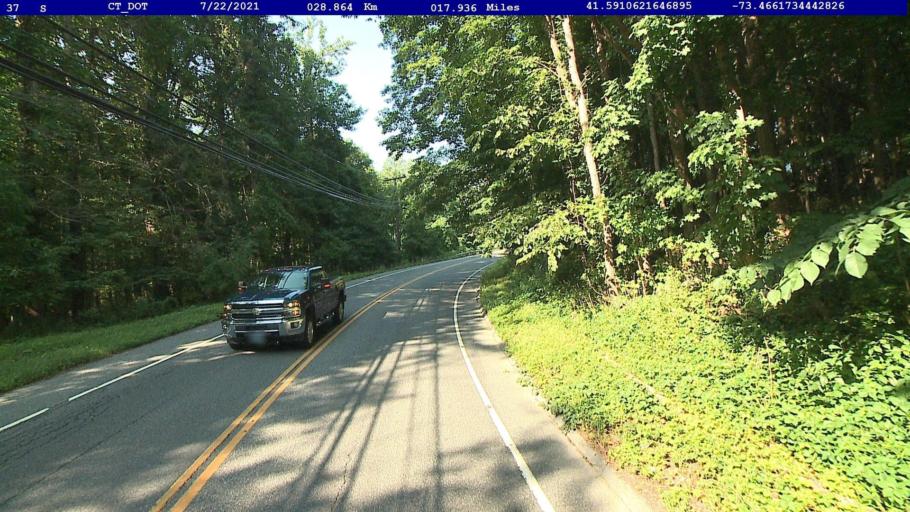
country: US
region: Connecticut
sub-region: Fairfield County
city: Sherman
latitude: 41.5909
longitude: -73.4662
